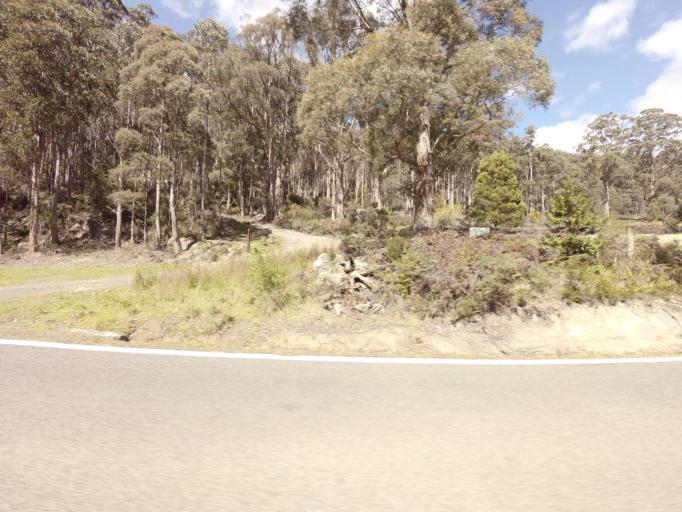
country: AU
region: Tasmania
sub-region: Derwent Valley
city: New Norfolk
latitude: -42.7054
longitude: 146.7123
